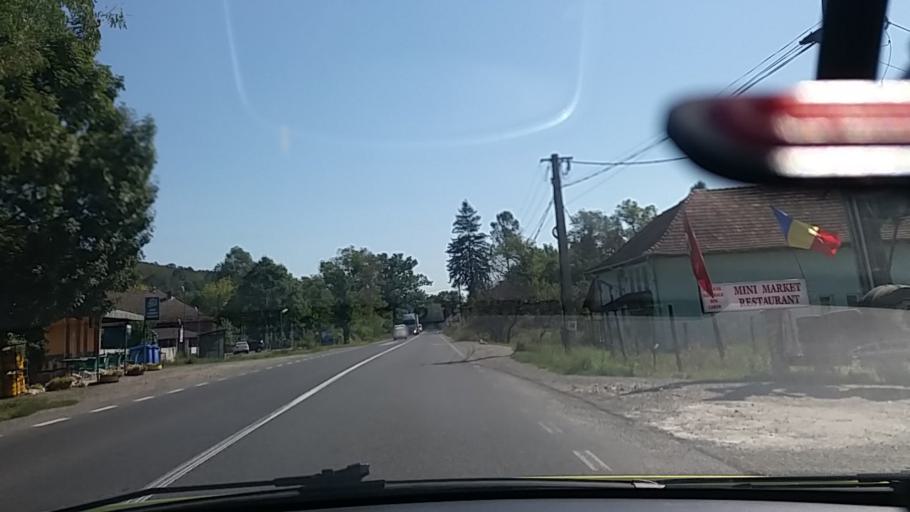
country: RO
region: Arad
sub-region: Comuna Petris
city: Petris
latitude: 46.0157
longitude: 22.3596
